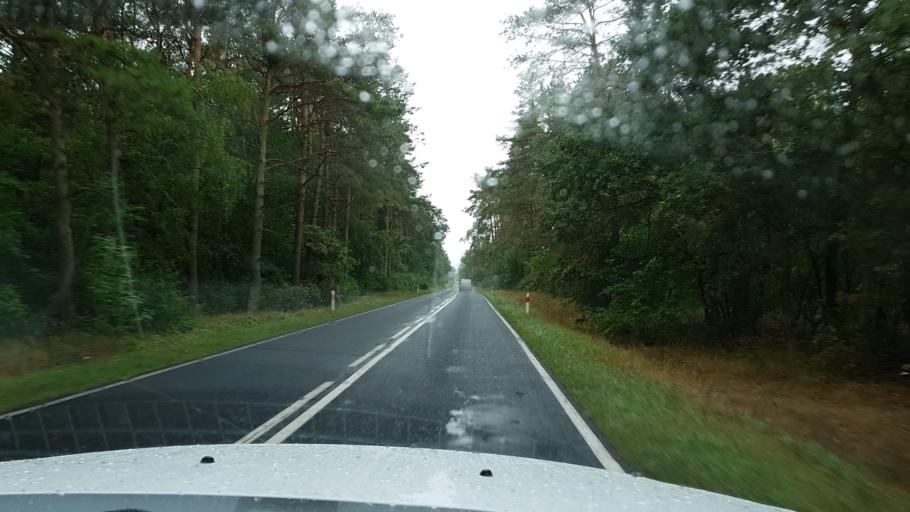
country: DE
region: Brandenburg
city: Schwedt (Oder)
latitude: 53.0511
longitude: 14.3463
